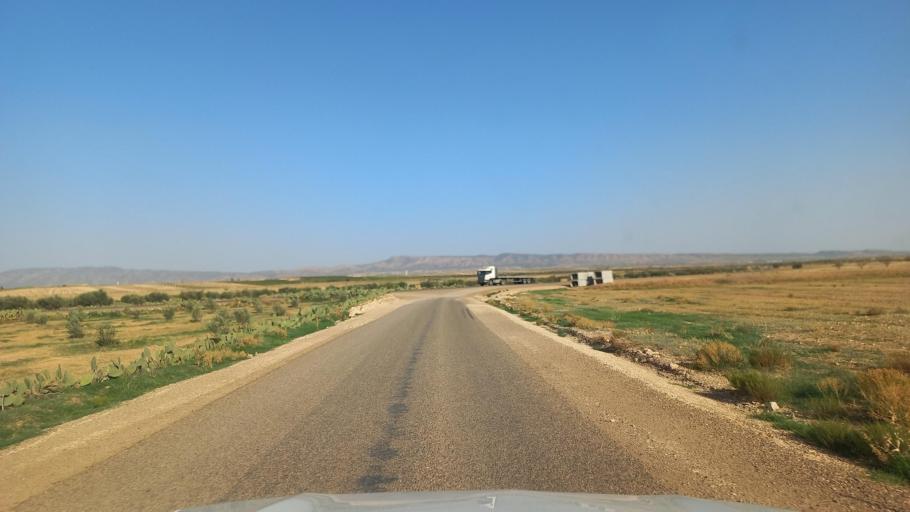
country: TN
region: Al Qasrayn
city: Sbiba
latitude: 35.3777
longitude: 9.0308
